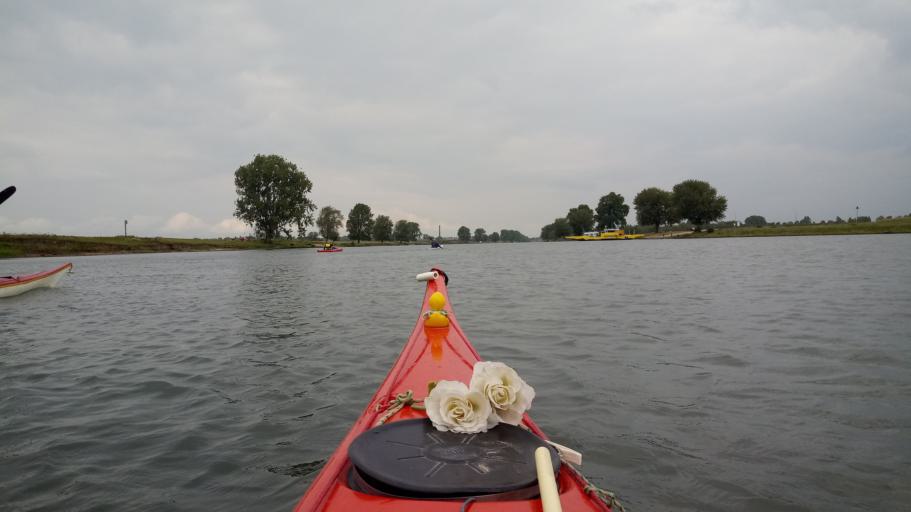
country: NL
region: Gelderland
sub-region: Gemeente Maasdriel
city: Heerewaarden
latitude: 51.7822
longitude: 5.3634
